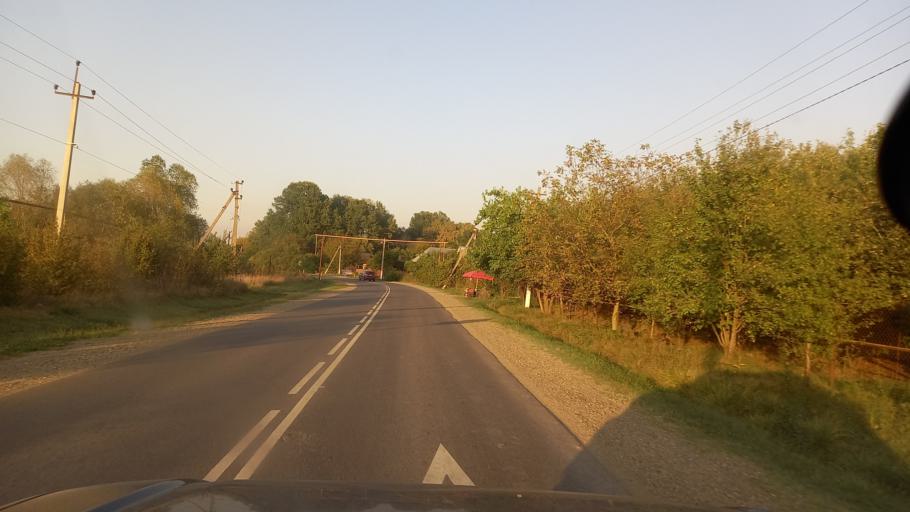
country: RU
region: Krasnodarskiy
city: Smolenskaya
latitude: 44.7649
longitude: 38.7767
